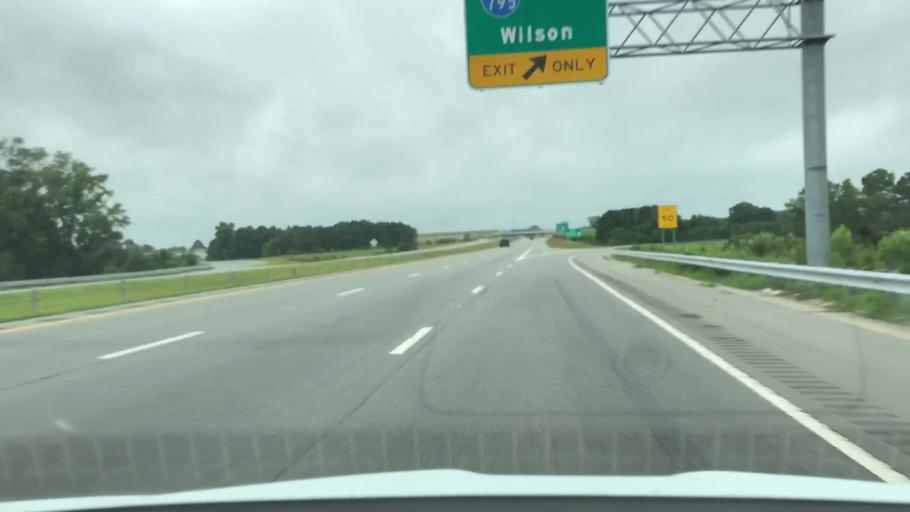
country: US
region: North Carolina
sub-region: Wayne County
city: Goldsboro
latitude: 35.4265
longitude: -77.9861
